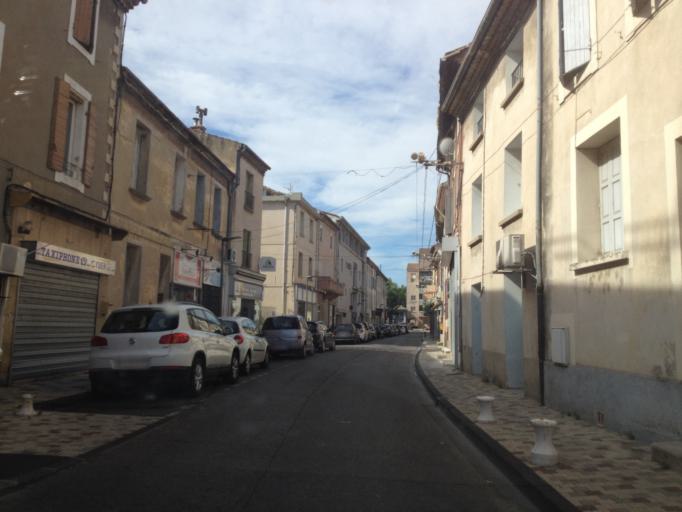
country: FR
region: Provence-Alpes-Cote d'Azur
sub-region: Departement du Vaucluse
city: Sorgues
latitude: 44.0111
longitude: 4.8730
